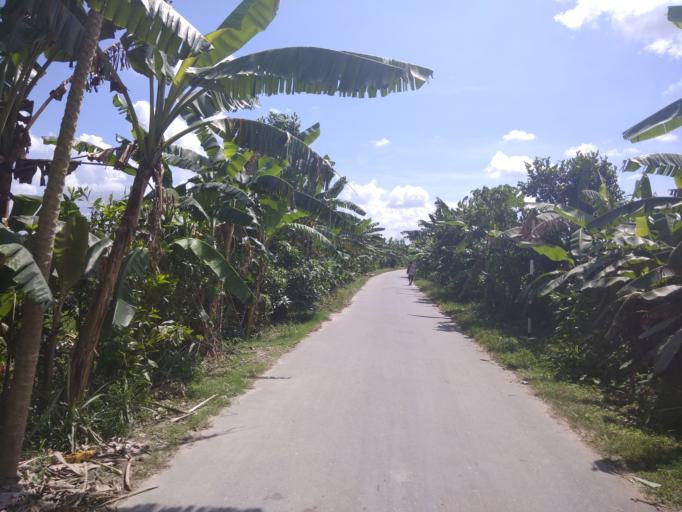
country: BD
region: Dhaka
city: Narayanganj
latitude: 23.4552
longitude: 90.4753
